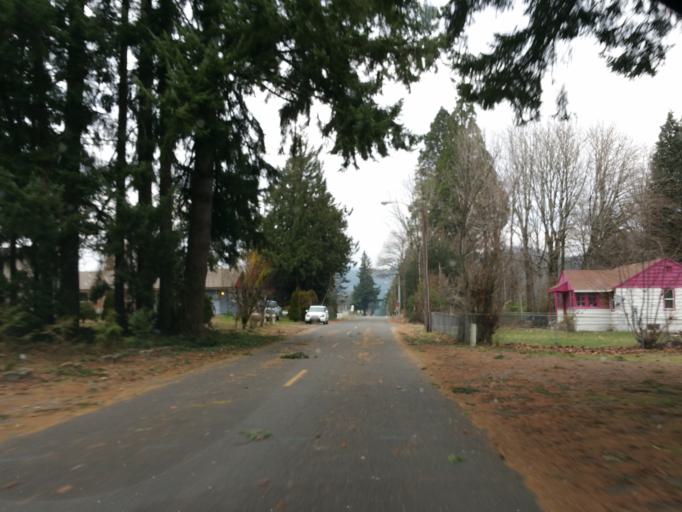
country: US
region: Washington
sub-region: Skamania County
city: Carson
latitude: 45.7246
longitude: -121.8099
